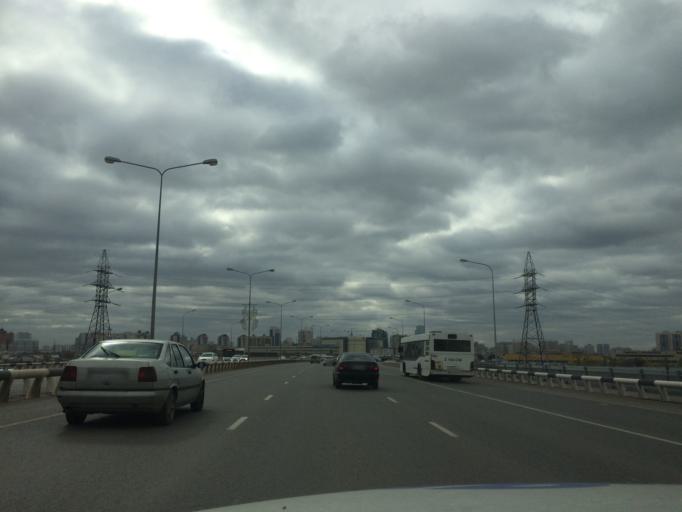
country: KZ
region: Astana Qalasy
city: Astana
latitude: 51.1830
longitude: 71.4450
